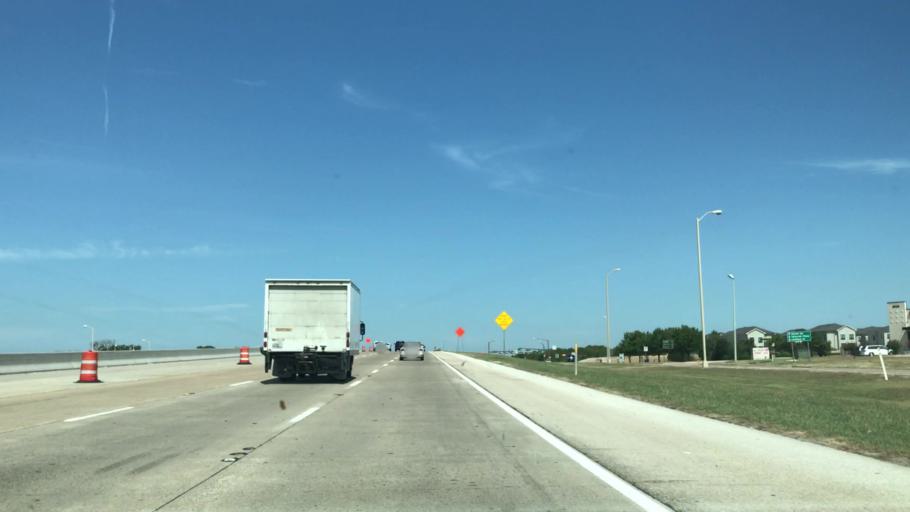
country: US
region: Texas
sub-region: Collin County
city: Murphy
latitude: 32.9734
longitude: -96.6536
